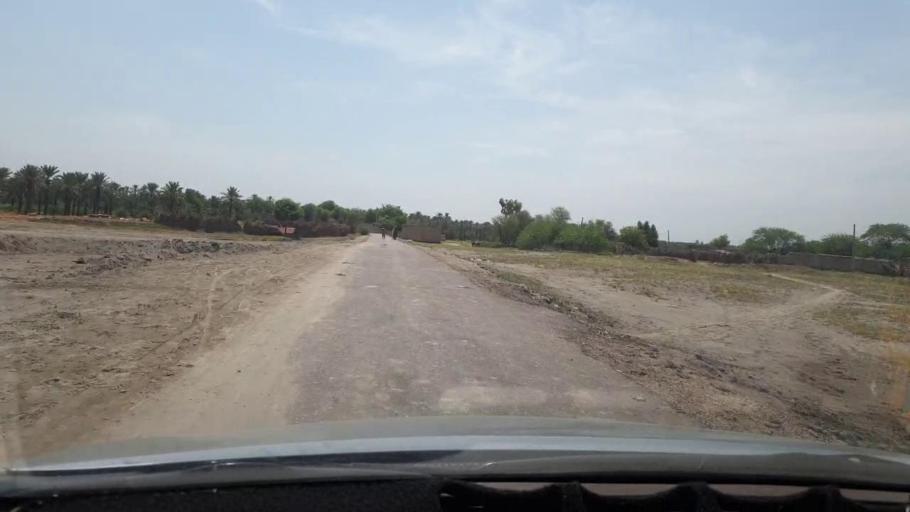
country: PK
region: Sindh
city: Khairpur
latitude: 27.4871
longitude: 68.7630
